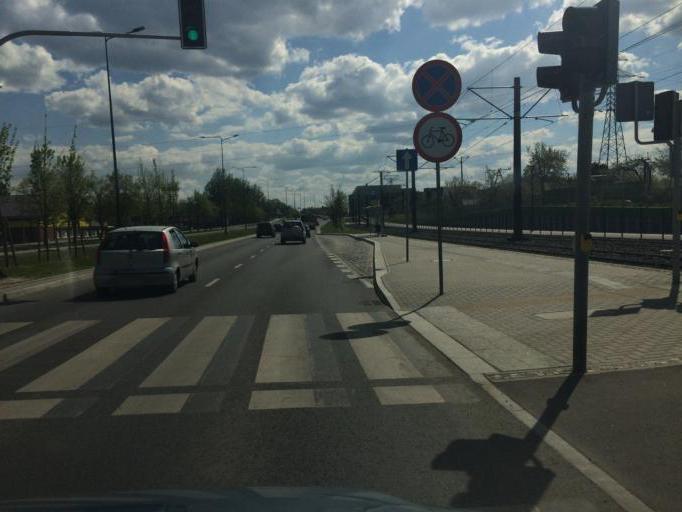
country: PL
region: Warmian-Masurian Voivodeship
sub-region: Powiat olsztynski
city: Olsztyn
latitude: 53.7593
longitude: 20.4866
